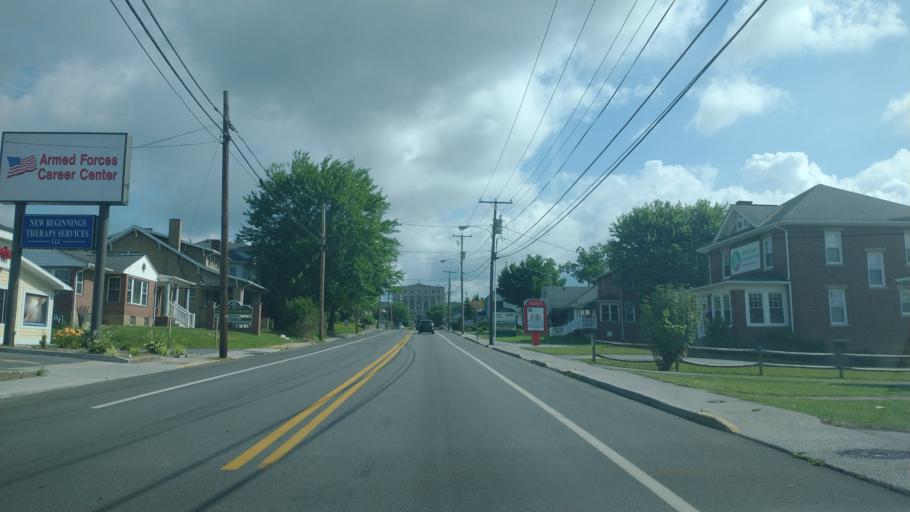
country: US
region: West Virginia
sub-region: Mercer County
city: Princeton
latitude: 37.3627
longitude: -81.1042
